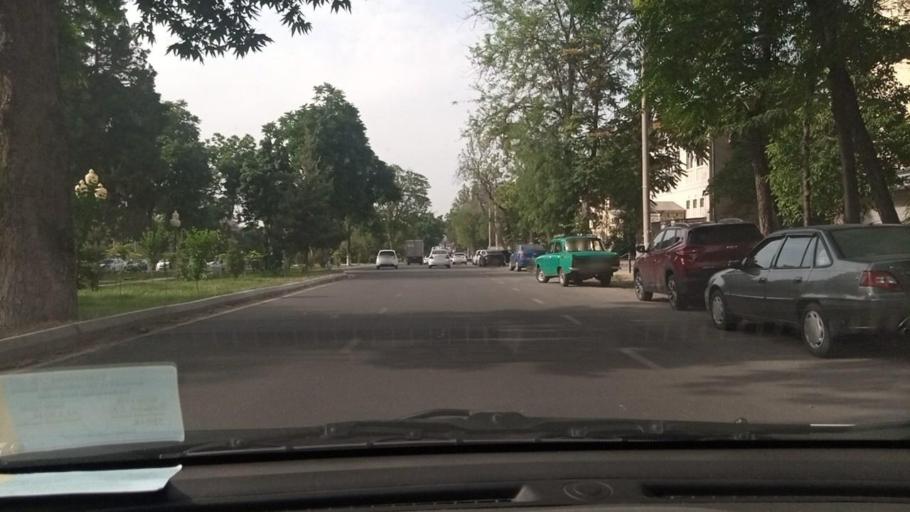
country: UZ
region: Toshkent Shahri
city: Tashkent
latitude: 41.3286
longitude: 69.2916
